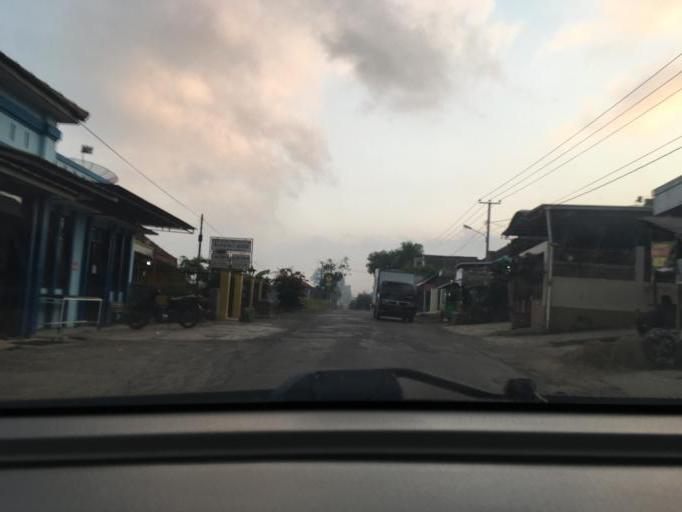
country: ID
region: West Java
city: Padamulya
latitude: -7.2100
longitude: 108.1997
